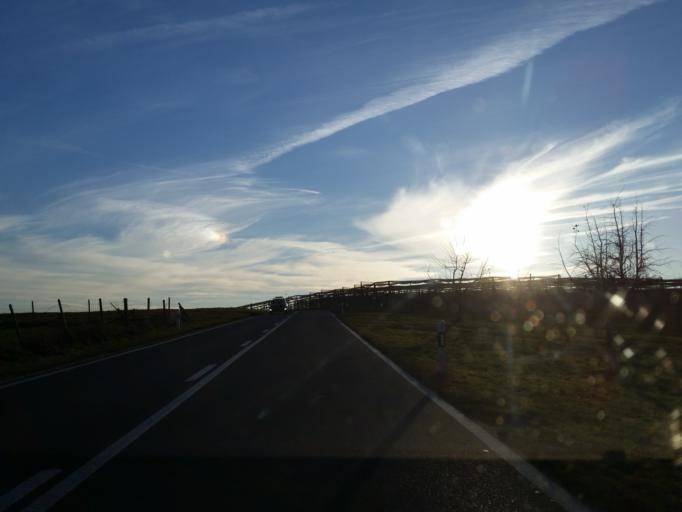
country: CH
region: Thurgau
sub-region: Weinfelden District
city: Erlen
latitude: 47.5306
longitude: 9.2618
